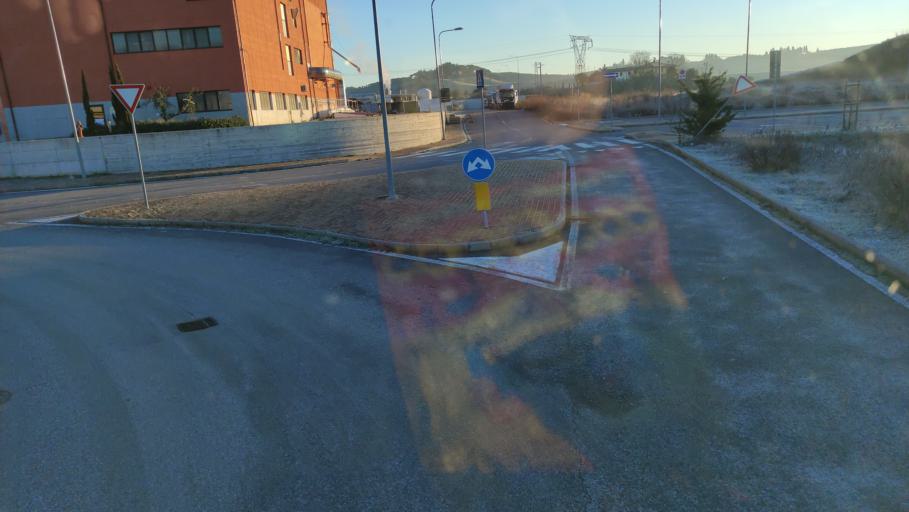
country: IT
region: Tuscany
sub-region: Province of Florence
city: Castelfiorentino
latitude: 43.6478
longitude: 10.9569
